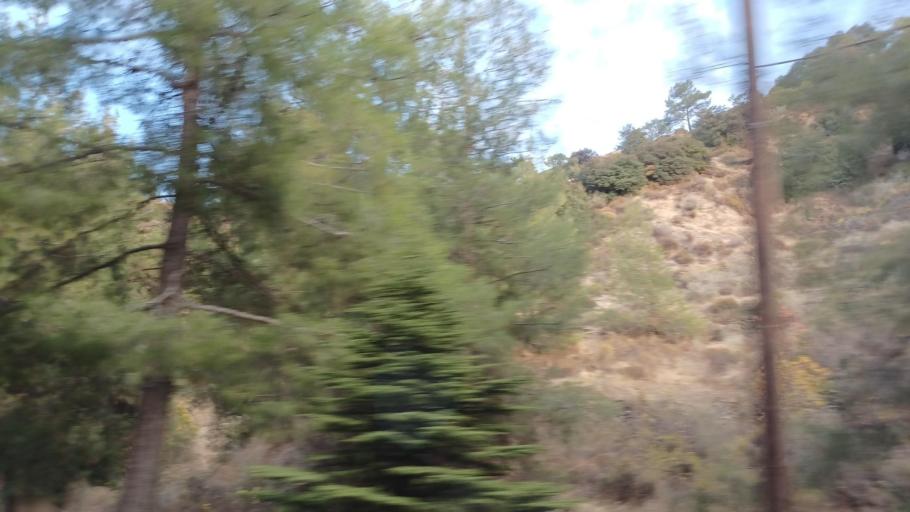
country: CY
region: Lefkosia
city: Kakopetria
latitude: 34.9853
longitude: 32.9067
